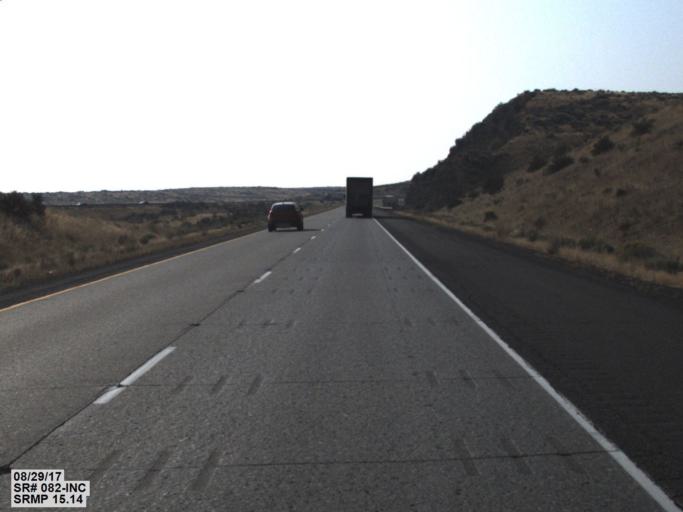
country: US
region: Washington
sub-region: Kittitas County
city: Kittitas
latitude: 46.7988
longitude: -120.3607
